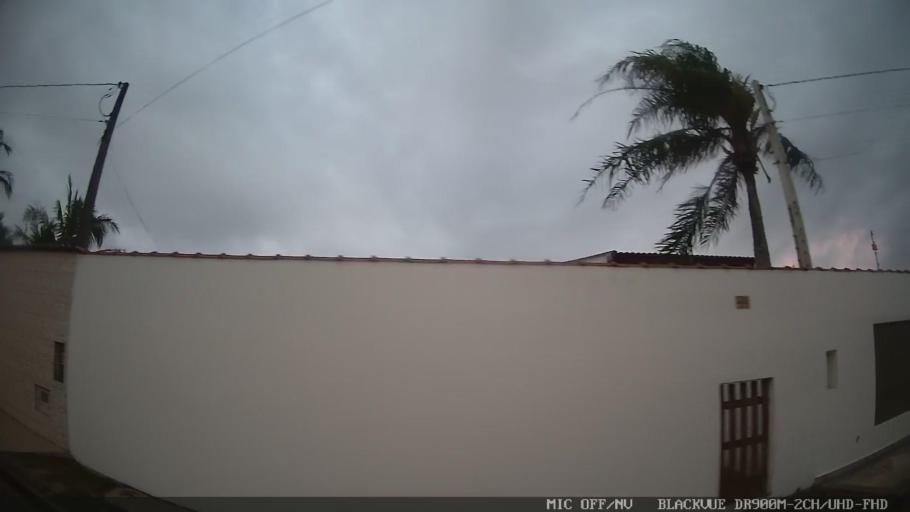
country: BR
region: Sao Paulo
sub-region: Itanhaem
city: Itanhaem
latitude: -24.2115
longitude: -46.8385
